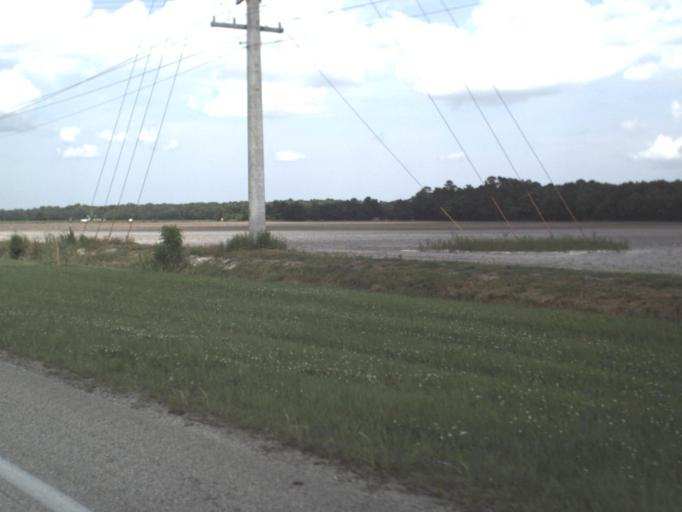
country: US
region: Florida
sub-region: Putnam County
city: East Palatka
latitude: 29.6954
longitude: -81.5603
